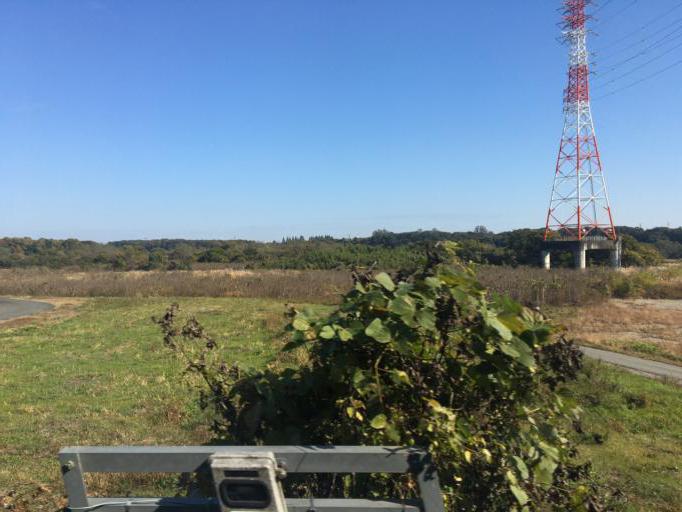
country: JP
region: Tochigi
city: Oyama
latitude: 36.3388
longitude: 139.8022
